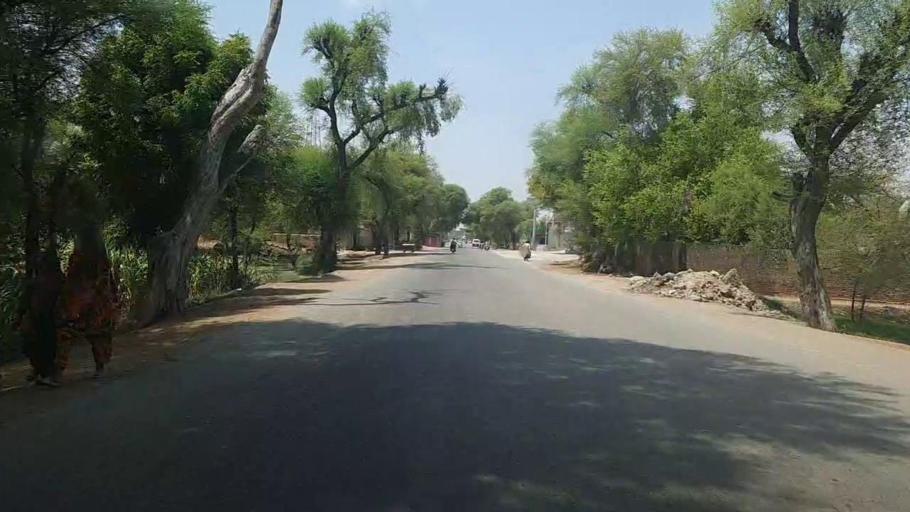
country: PK
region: Sindh
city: Ubauro
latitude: 28.3158
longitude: 69.7987
